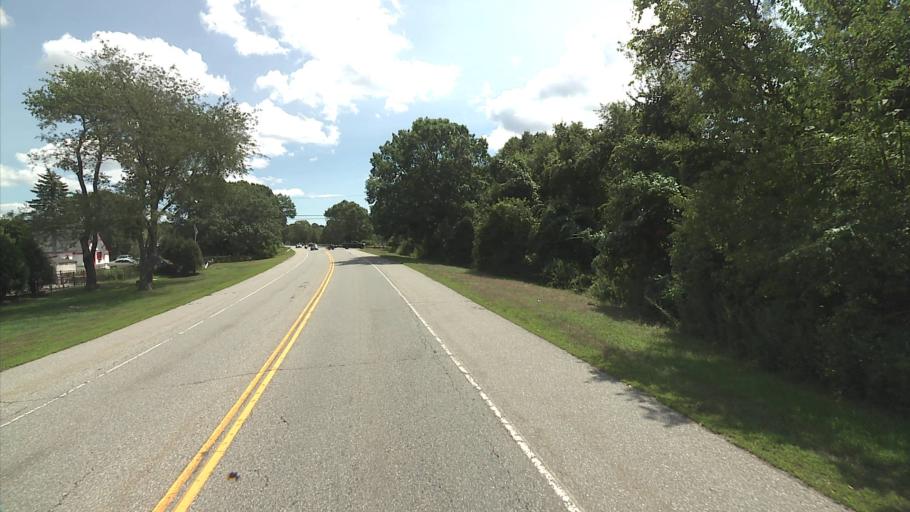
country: US
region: Connecticut
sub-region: New London County
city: Mystic
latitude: 41.3433
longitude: -71.9495
